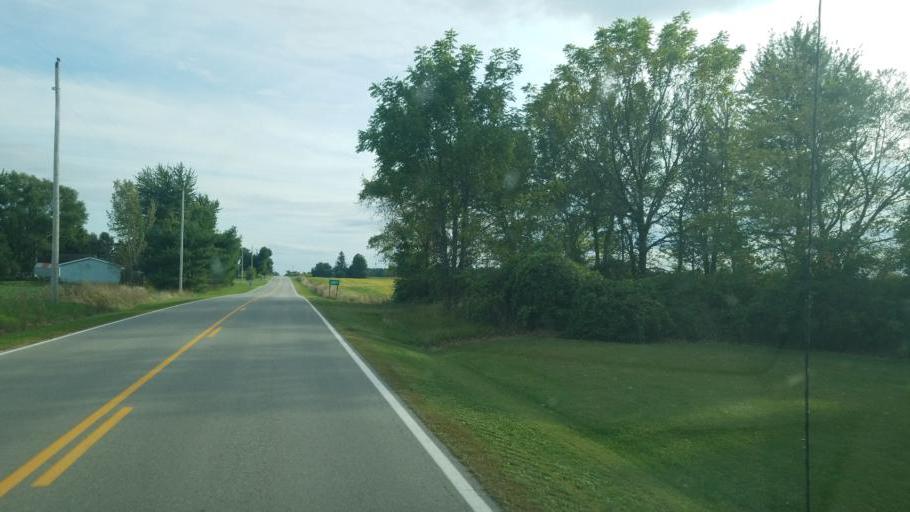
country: US
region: Ohio
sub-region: Crawford County
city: Bucyrus
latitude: 40.8964
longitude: -83.0935
